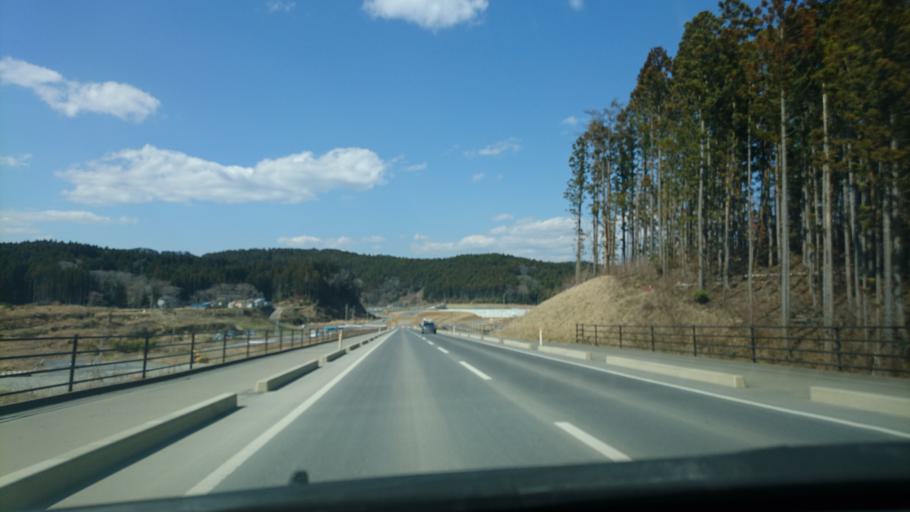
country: JP
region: Miyagi
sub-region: Oshika Gun
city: Onagawa Cho
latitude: 38.6414
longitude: 141.4389
